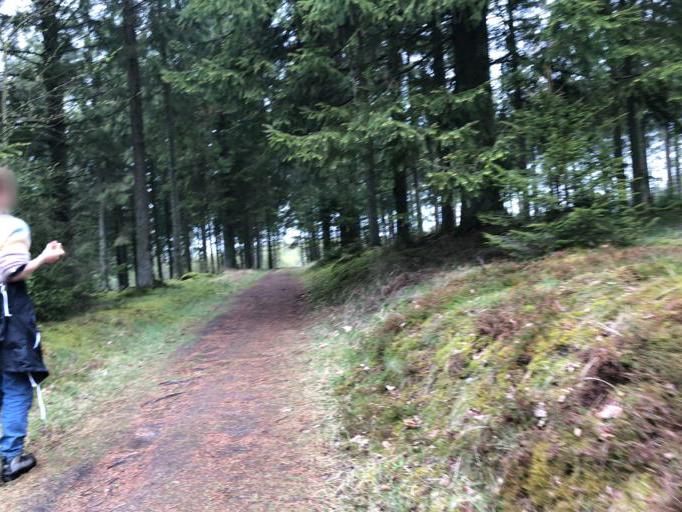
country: DK
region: Central Jutland
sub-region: Lemvig Kommune
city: Lemvig
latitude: 56.4783
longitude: 8.3610
